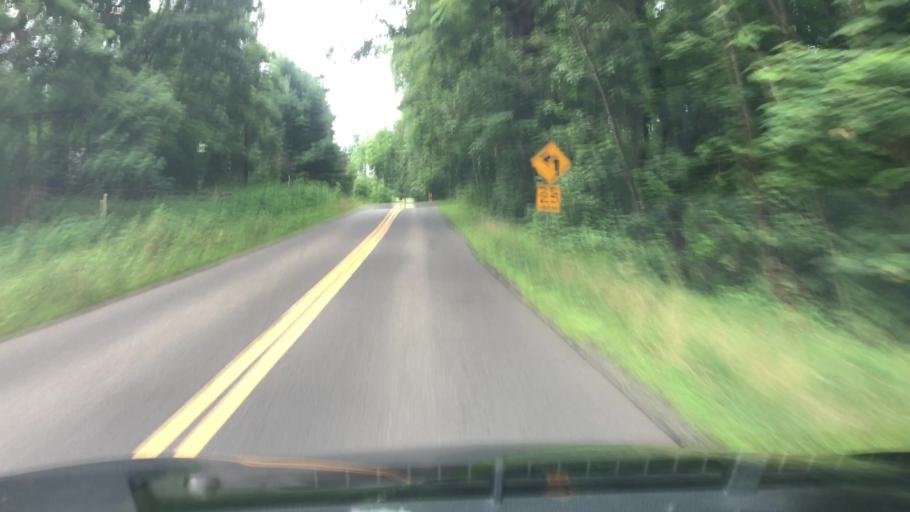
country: US
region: Virginia
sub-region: Fauquier County
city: New Baltimore
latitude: 38.7487
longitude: -77.6878
